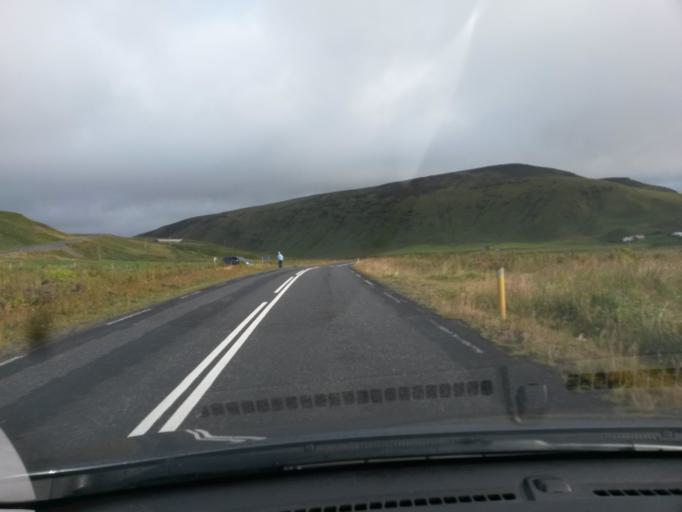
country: IS
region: South
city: Vestmannaeyjar
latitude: 63.4447
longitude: -19.1401
